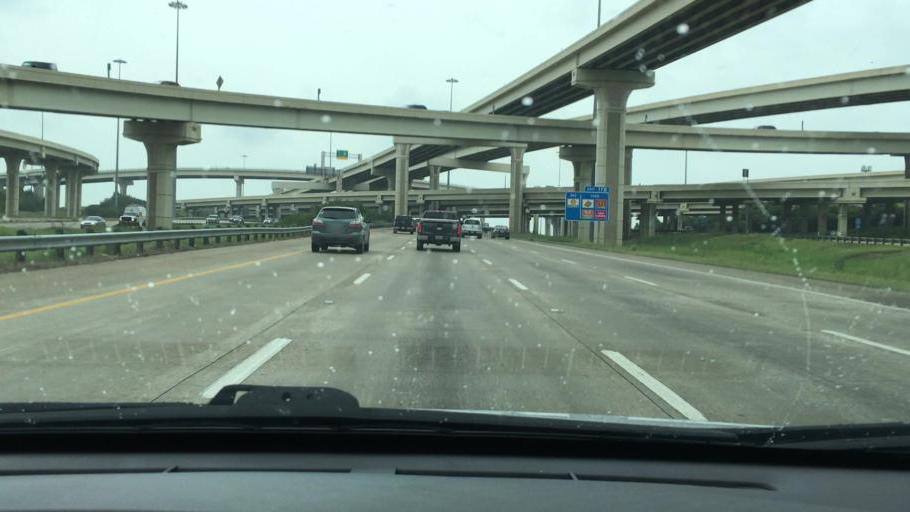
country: US
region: Texas
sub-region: Bexar County
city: Balcones Heights
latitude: 29.4988
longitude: -98.5502
